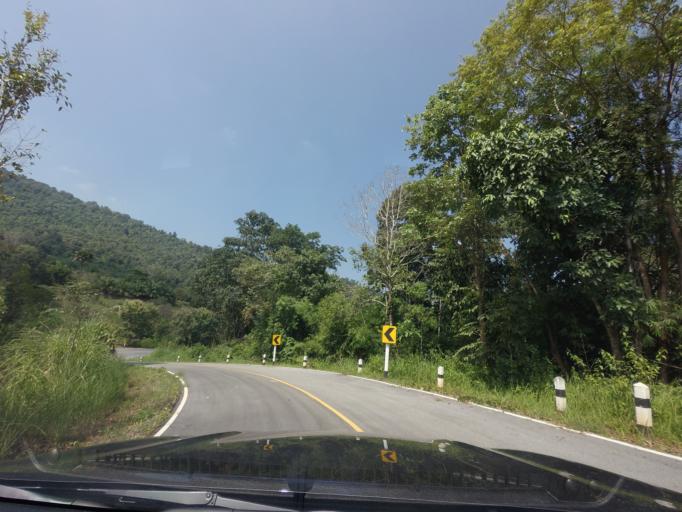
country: TH
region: Loei
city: Na Haeo
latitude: 17.5654
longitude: 100.9858
